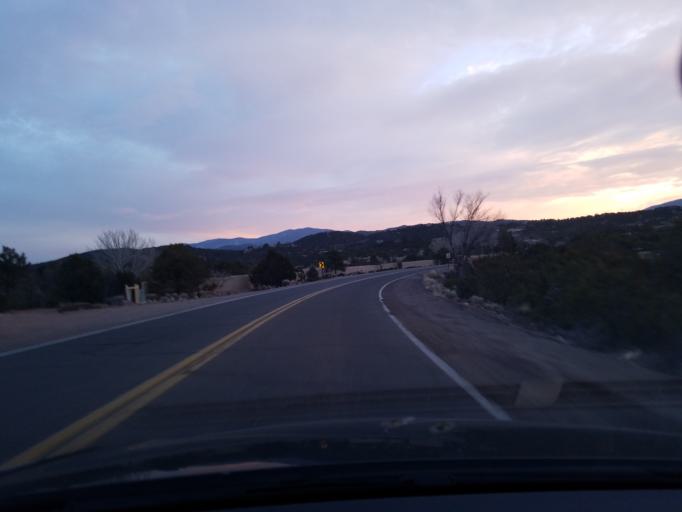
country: US
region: New Mexico
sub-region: Santa Fe County
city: Santa Fe
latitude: 35.6947
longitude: -105.9191
